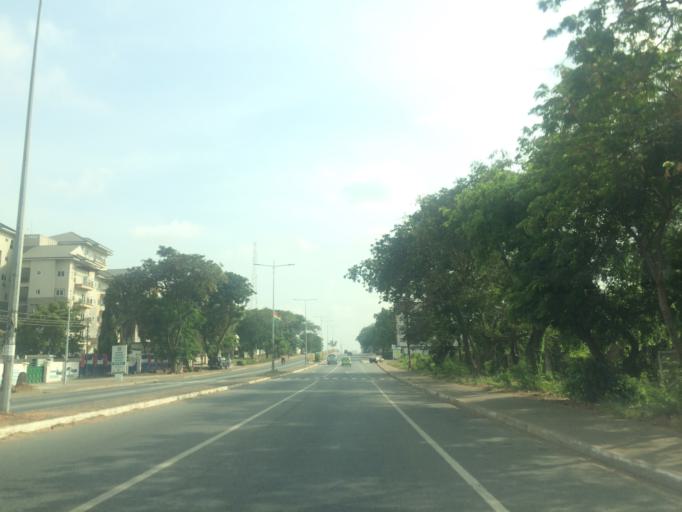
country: GH
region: Greater Accra
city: Accra
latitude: 5.5670
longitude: -0.2018
